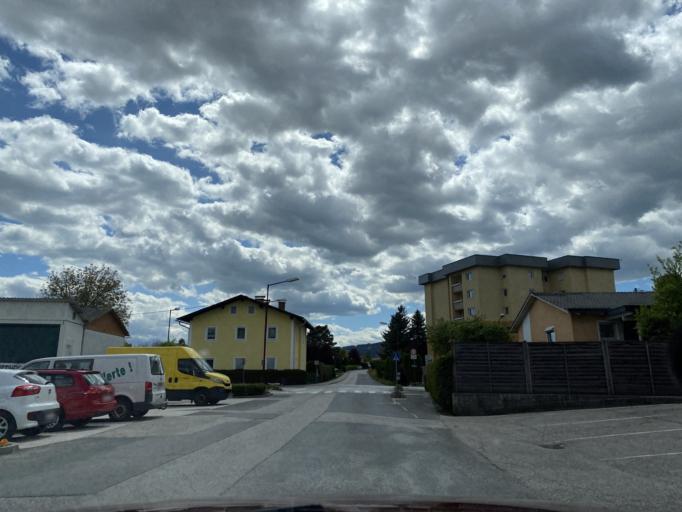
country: AT
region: Carinthia
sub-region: Politischer Bezirk Wolfsberg
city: Wolfsberg
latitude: 46.8294
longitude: 14.8341
